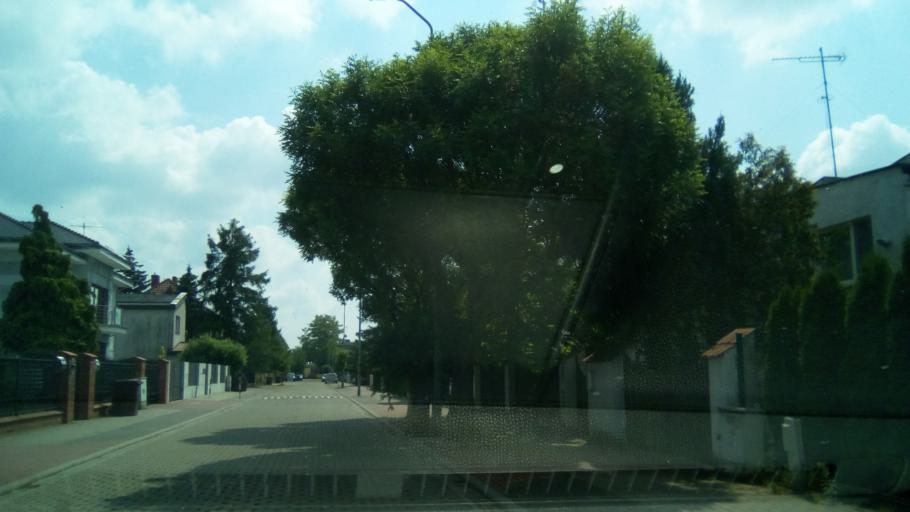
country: PL
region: Greater Poland Voivodeship
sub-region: Powiat gnieznienski
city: Gniezno
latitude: 52.5354
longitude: 17.6220
